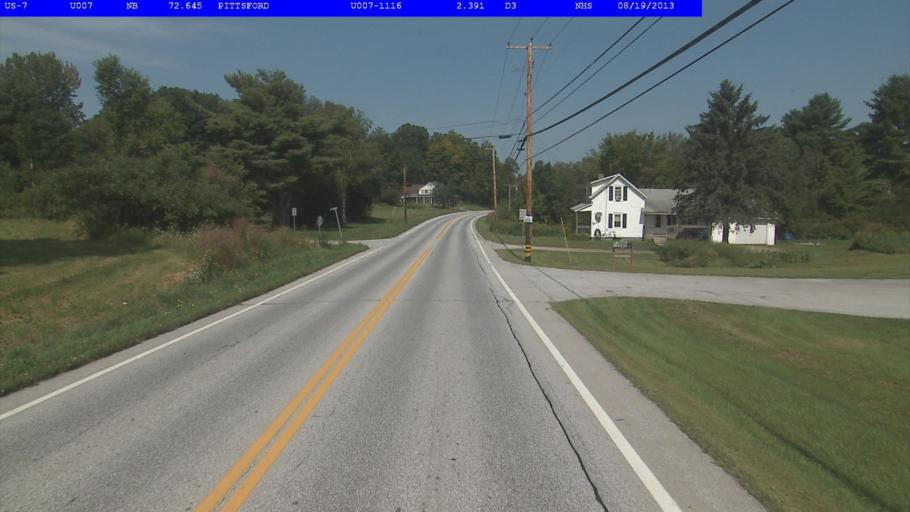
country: US
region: Vermont
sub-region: Rutland County
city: Rutland
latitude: 43.6961
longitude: -73.0041
